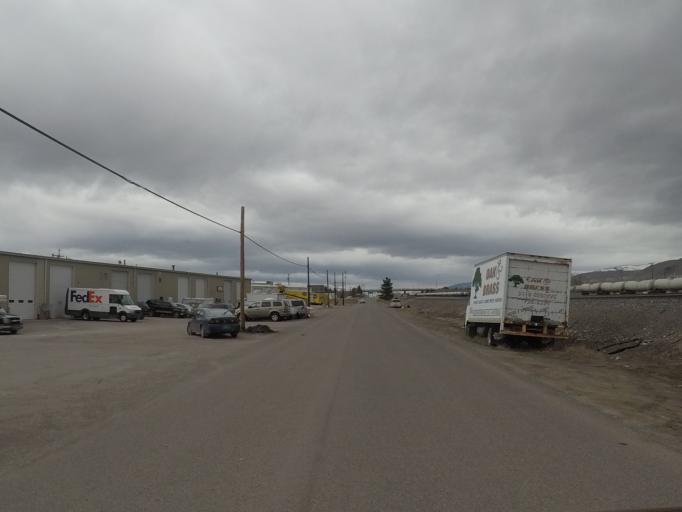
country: US
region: Montana
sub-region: Missoula County
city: Orchard Homes
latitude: 46.8943
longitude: -114.0303
